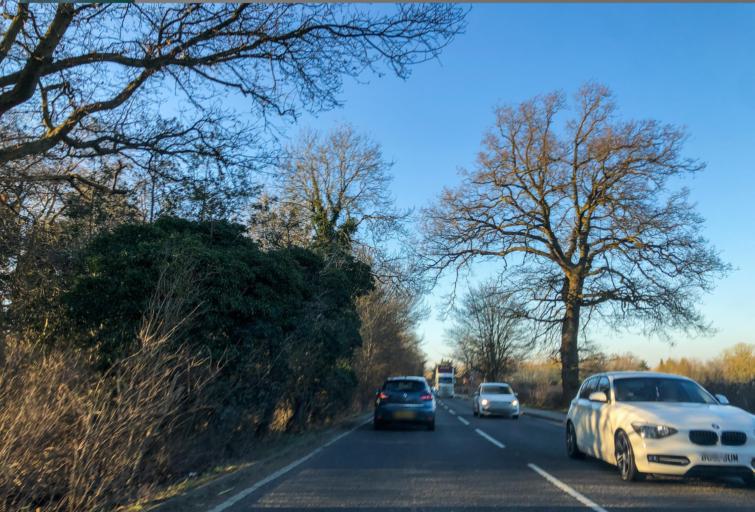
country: GB
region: England
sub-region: Warwickshire
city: Warwick
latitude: 52.2513
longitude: -1.6126
